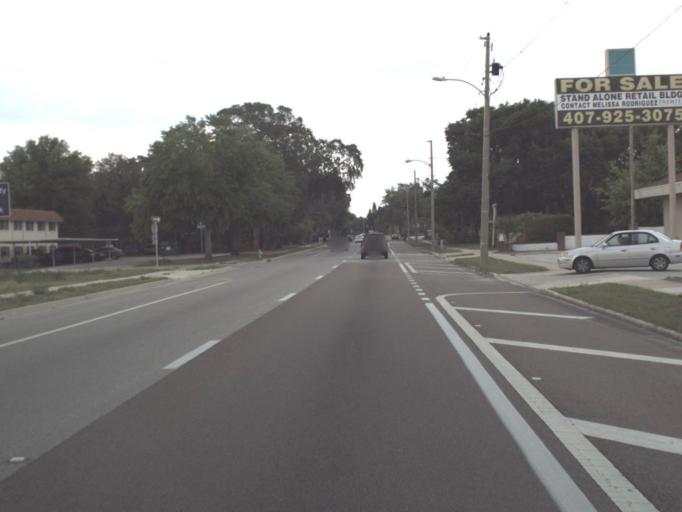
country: US
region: Florida
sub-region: Lake County
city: Eustis
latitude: 28.8577
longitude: -81.6836
